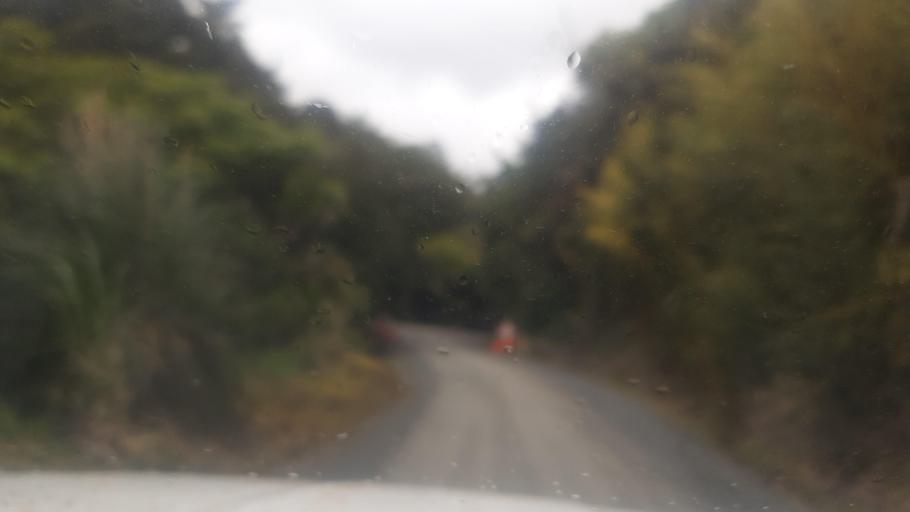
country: NZ
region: Northland
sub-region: Far North District
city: Taipa
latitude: -35.0924
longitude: 173.3947
